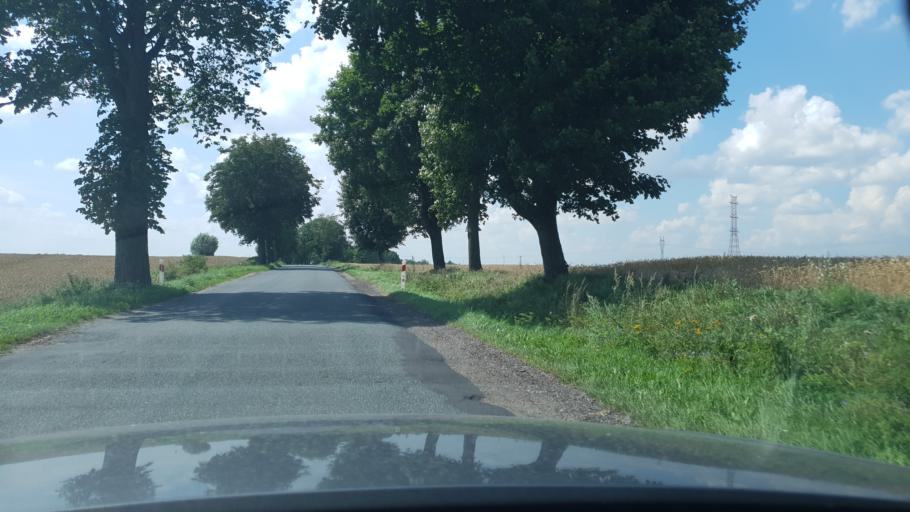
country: PL
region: Kujawsko-Pomorskie
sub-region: Powiat wabrzeski
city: Pluznica
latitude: 53.3737
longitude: 18.8197
